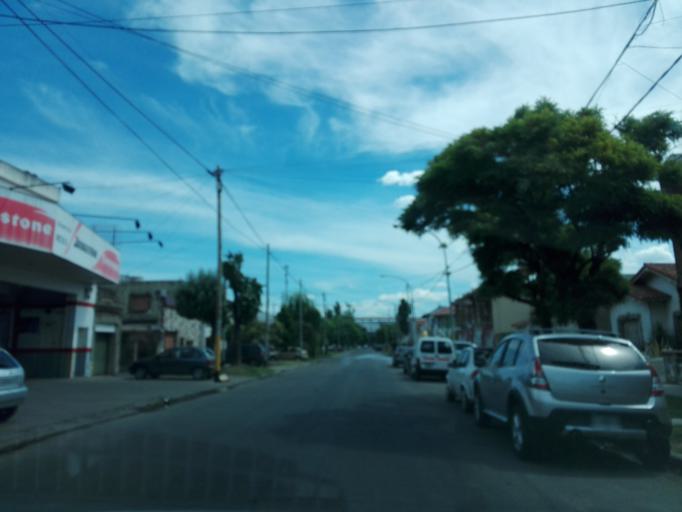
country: AR
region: Buenos Aires
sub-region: Partido de Lanus
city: Lanus
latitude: -34.7148
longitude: -58.3810
